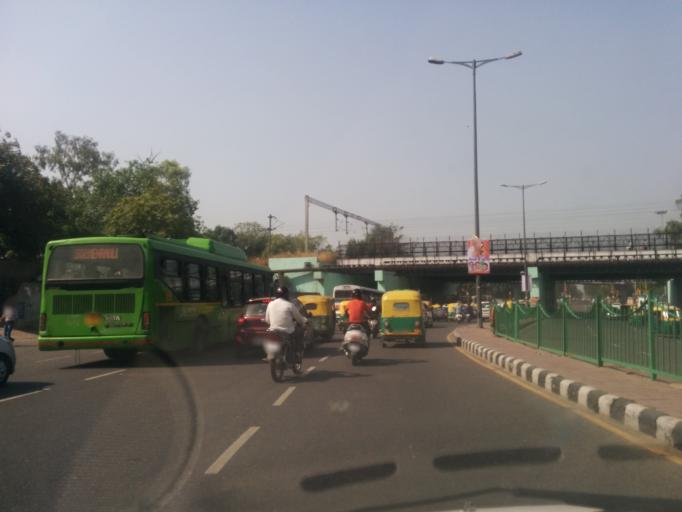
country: IN
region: NCT
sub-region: New Delhi
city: New Delhi
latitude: 28.6267
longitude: 77.2414
